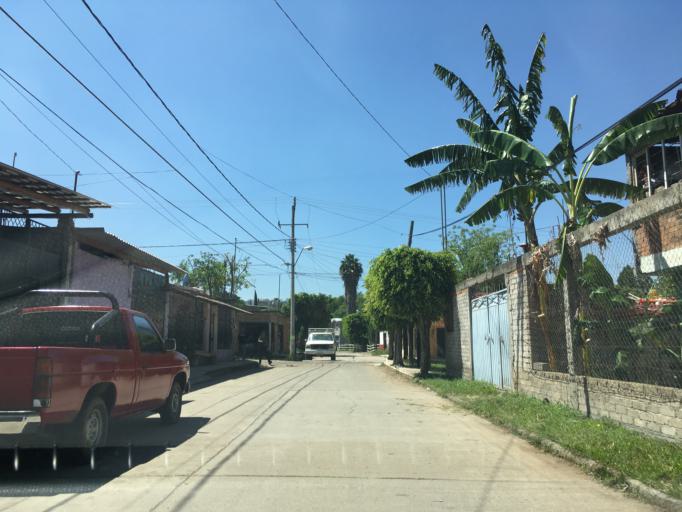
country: MX
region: Michoacan
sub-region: Morelia
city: Morelos
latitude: 19.6507
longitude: -101.2343
